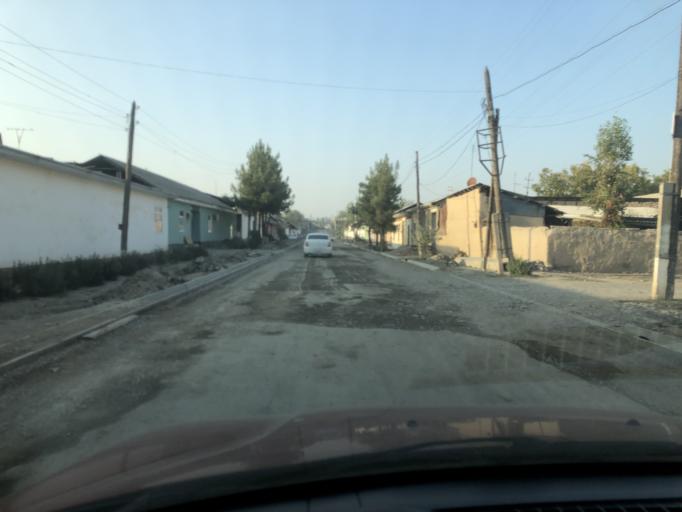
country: UZ
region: Namangan
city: Uychi
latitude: 41.0790
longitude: 72.0013
